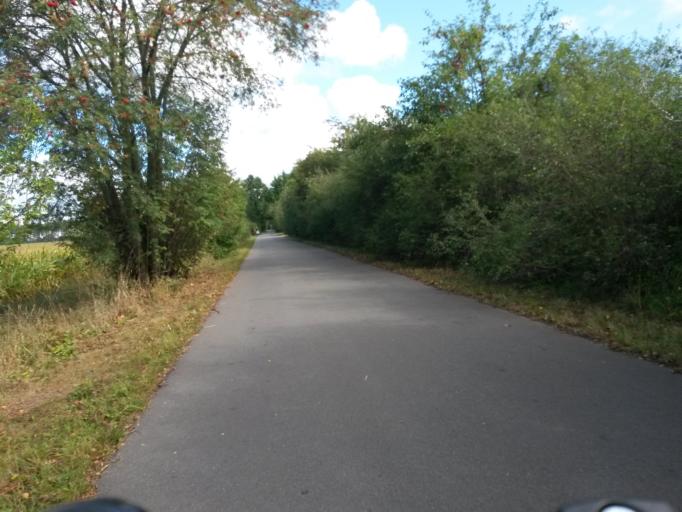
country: DE
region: Brandenburg
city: Templin
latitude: 53.2009
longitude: 13.5154
